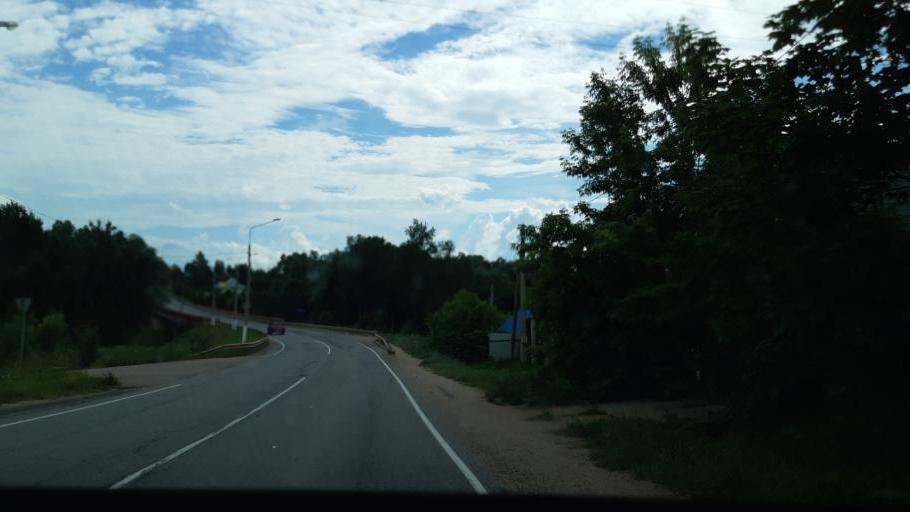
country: RU
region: Kaluga
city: Medyn'
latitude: 55.1048
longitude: 35.9513
